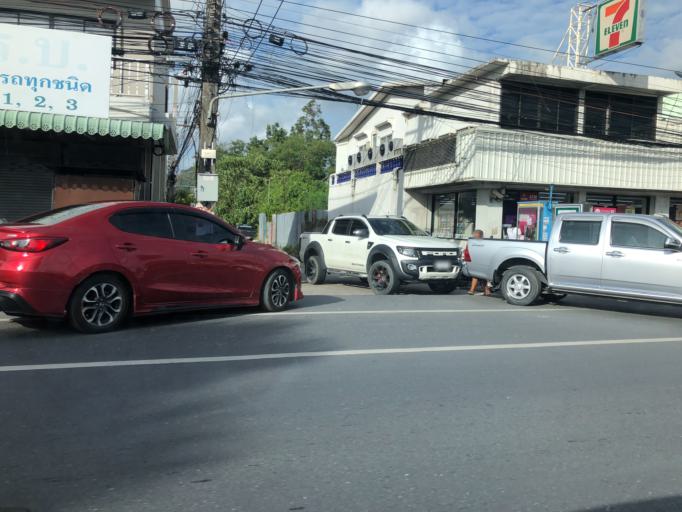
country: TH
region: Phuket
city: Thalang
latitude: 7.9967
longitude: 98.3507
